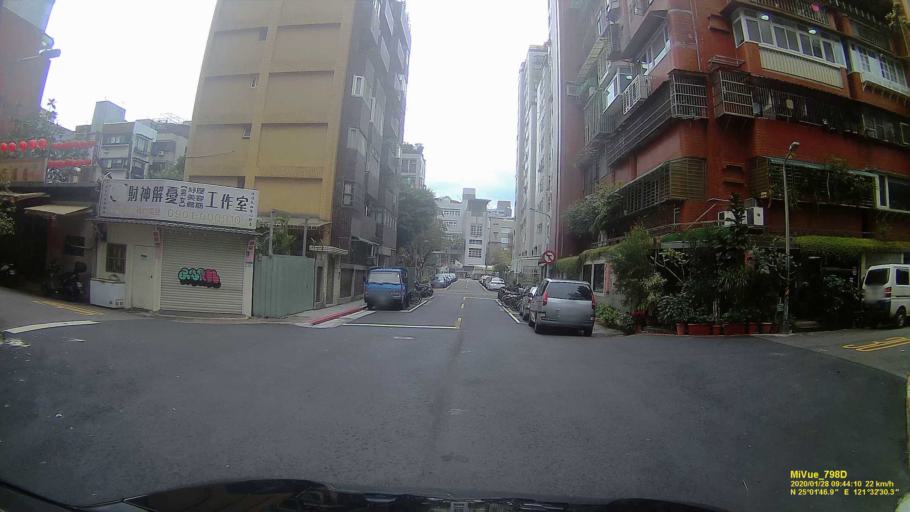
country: TW
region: Taipei
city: Taipei
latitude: 25.0298
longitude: 121.5419
